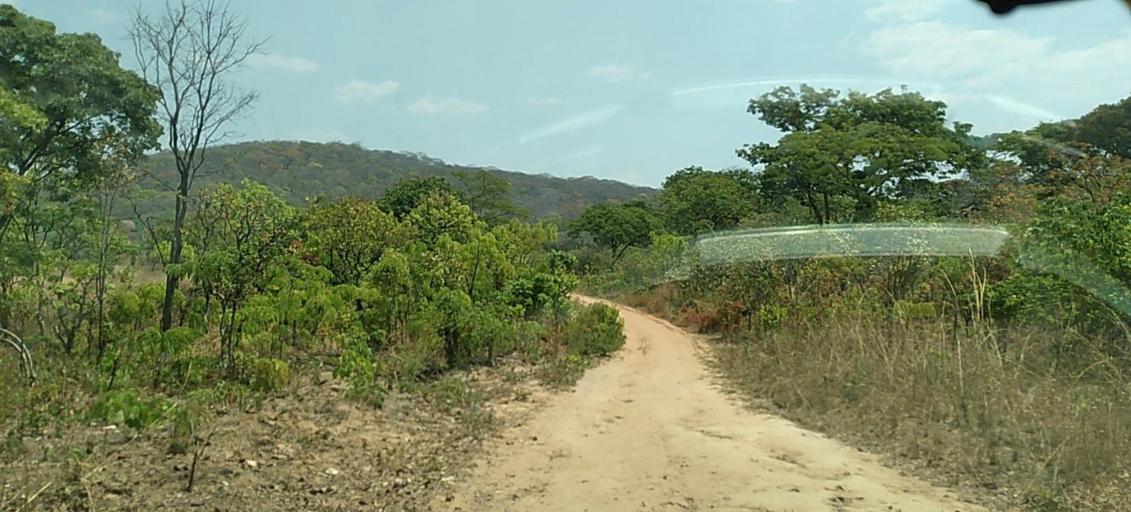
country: ZM
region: North-Western
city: Kasempa
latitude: -13.5258
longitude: 25.8248
